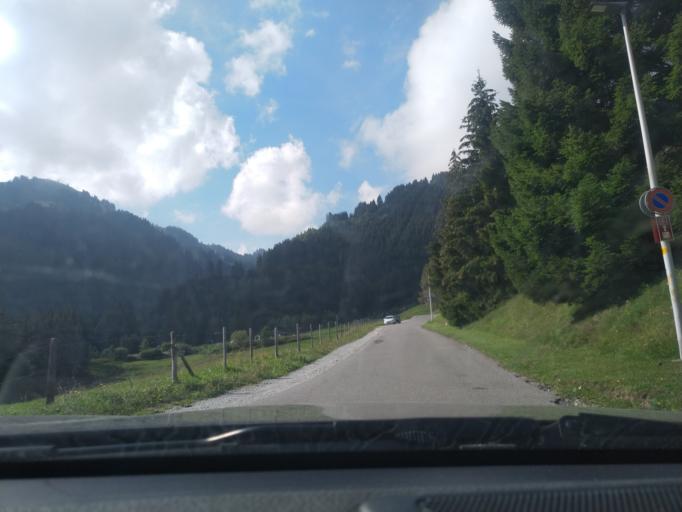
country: CH
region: Fribourg
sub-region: Gruyere District
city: Gruyeres
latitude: 46.5651
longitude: 7.0382
